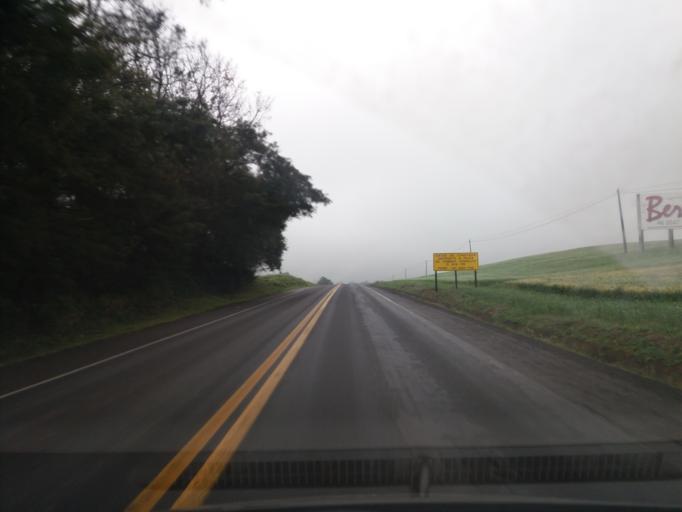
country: BR
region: Parana
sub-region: Ampere
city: Ampere
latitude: -25.8966
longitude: -53.4548
